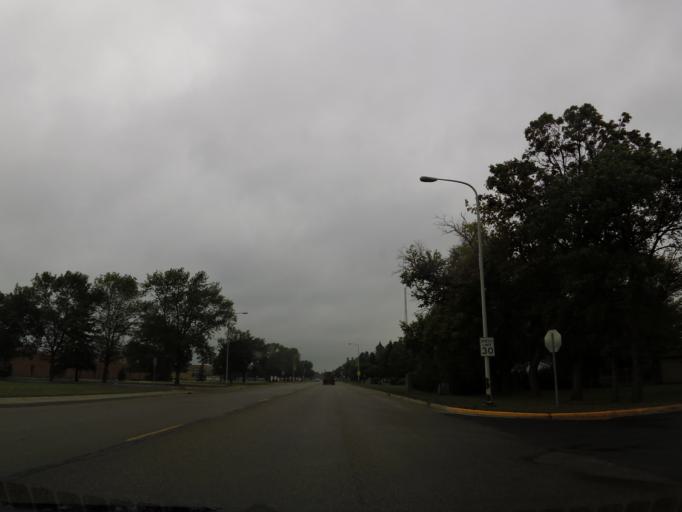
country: US
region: Minnesota
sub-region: Marshall County
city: Warren
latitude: 48.1951
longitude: -96.7638
